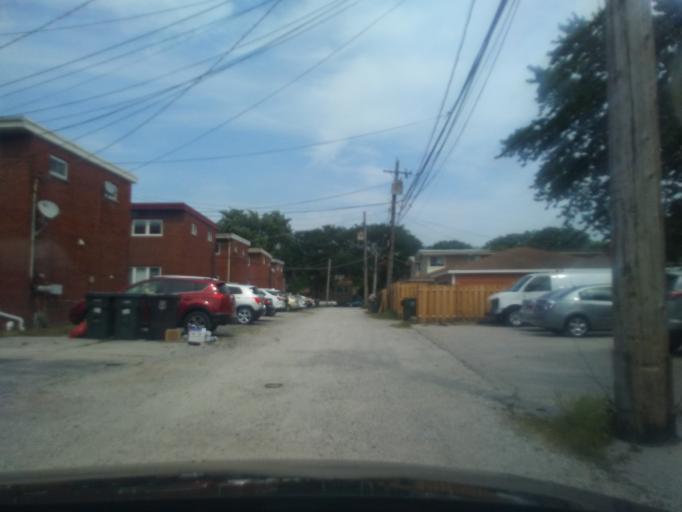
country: US
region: Illinois
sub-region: Cook County
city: Skokie
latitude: 42.0204
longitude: -87.7453
